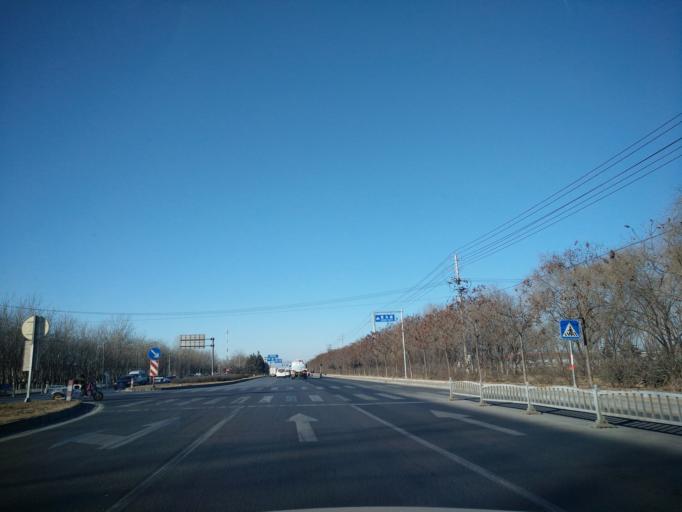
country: CN
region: Beijing
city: Xingfeng
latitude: 39.7204
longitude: 116.3762
